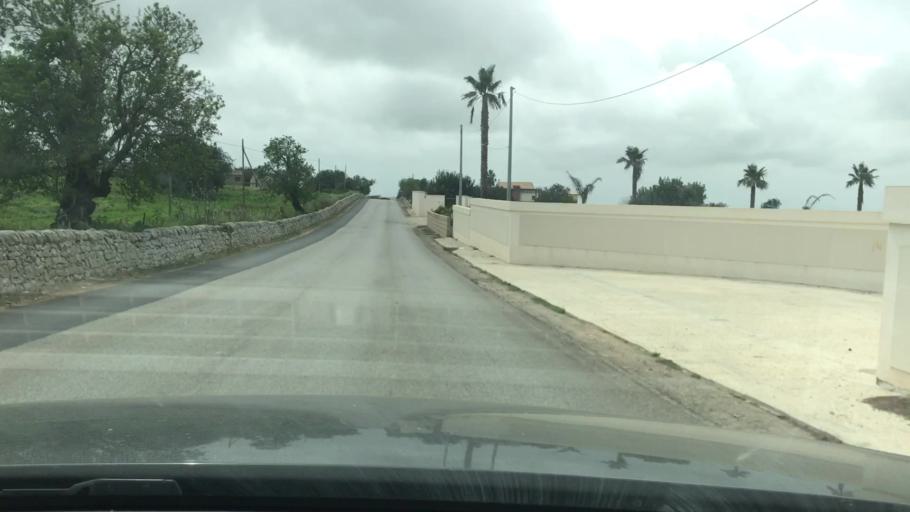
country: IT
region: Sicily
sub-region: Ragusa
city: Modica
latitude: 36.8218
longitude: 14.7475
